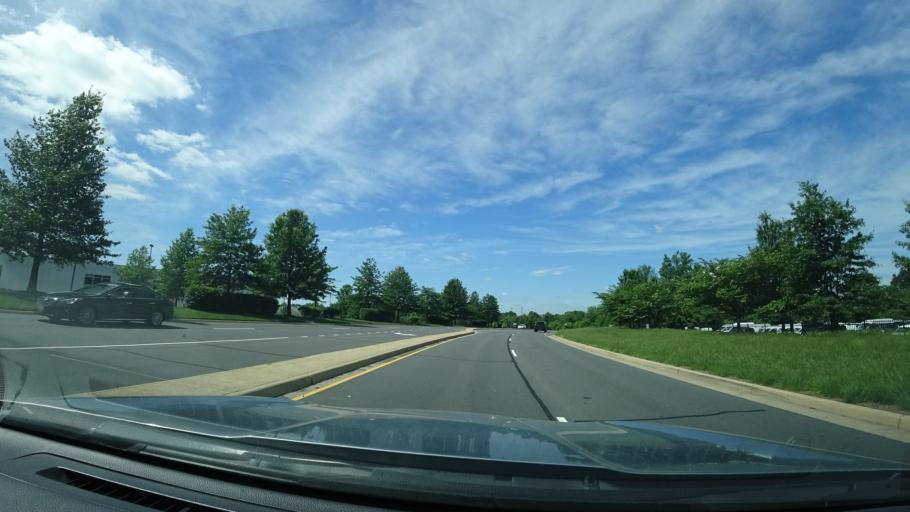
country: US
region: Virginia
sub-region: Loudoun County
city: Sterling
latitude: 39.0187
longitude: -77.4250
